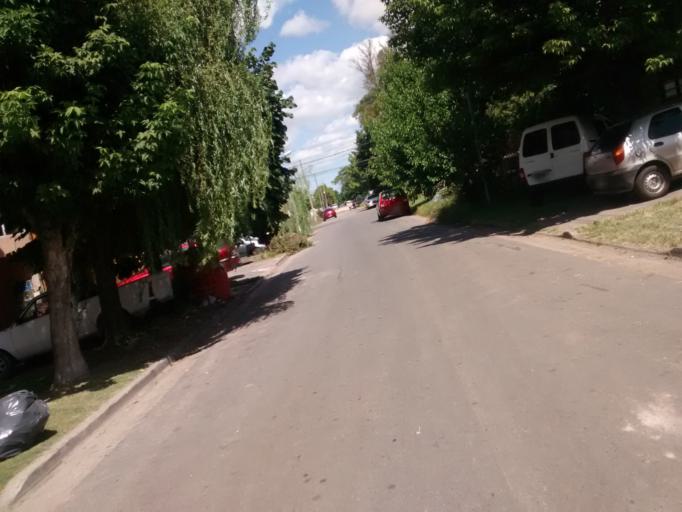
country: AR
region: Buenos Aires
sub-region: Partido de La Plata
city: La Plata
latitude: -34.9437
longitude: -57.9737
